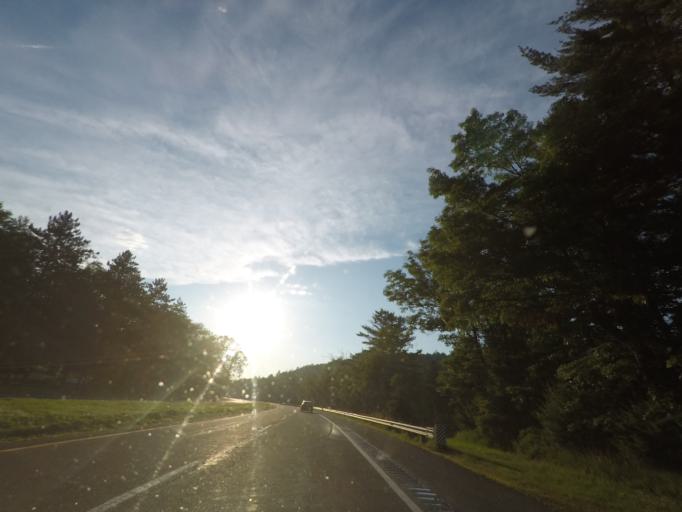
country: US
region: Massachusetts
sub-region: Hampden County
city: Brimfield
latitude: 42.1179
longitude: -72.2372
